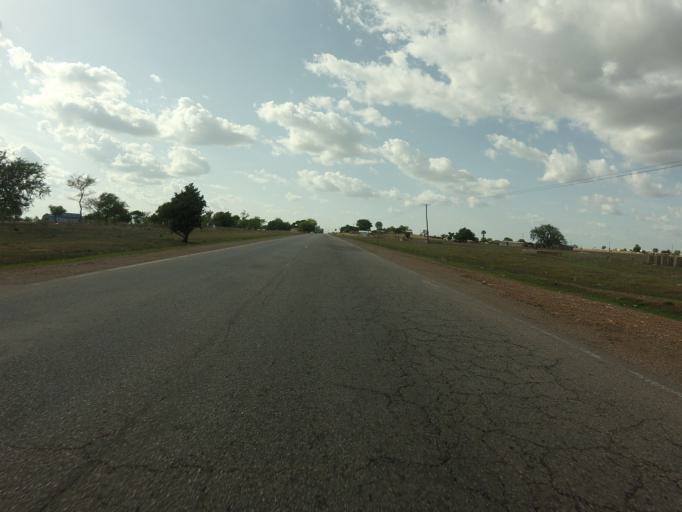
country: GH
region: Upper East
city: Bolgatanga
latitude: 10.6758
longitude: -0.8615
